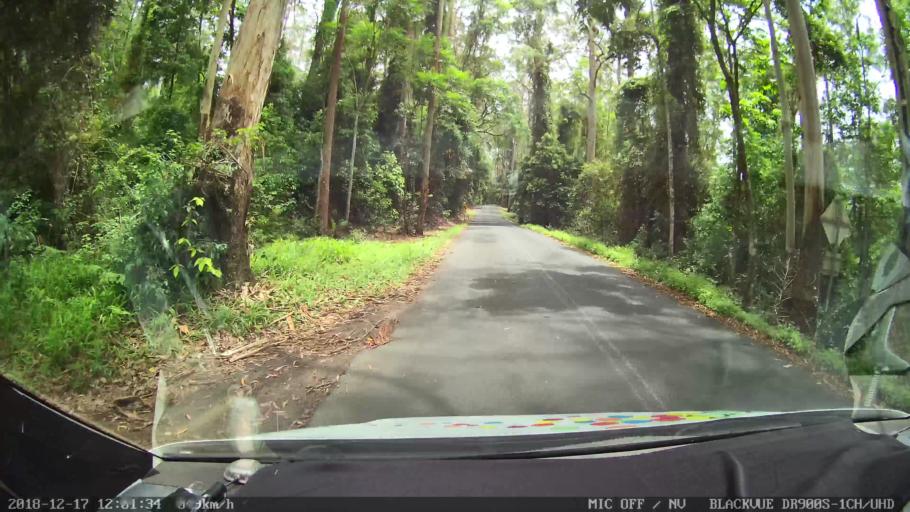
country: AU
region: New South Wales
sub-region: Kyogle
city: Kyogle
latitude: -28.5209
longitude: 152.5713
